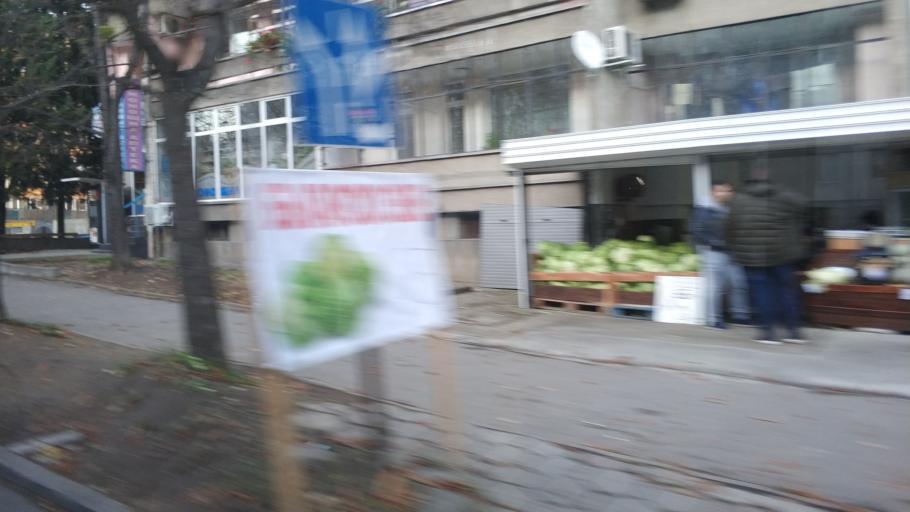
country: BG
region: Stara Zagora
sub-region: Obshtina Stara Zagora
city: Stara Zagora
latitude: 42.4197
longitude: 25.6198
